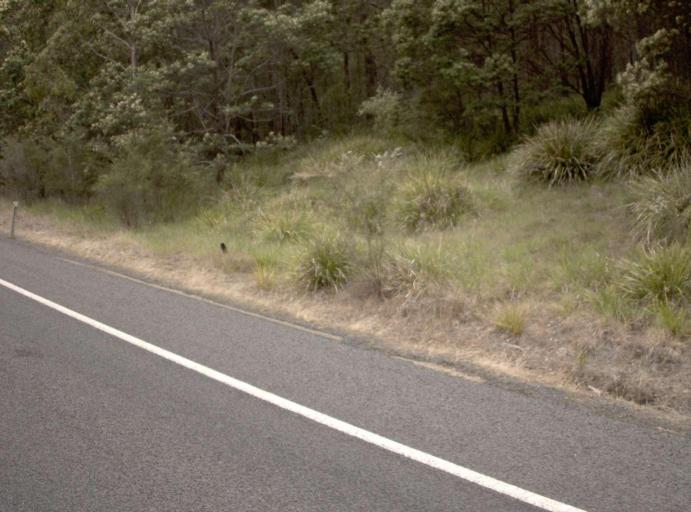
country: AU
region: New South Wales
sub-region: Bombala
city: Bombala
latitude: -37.2300
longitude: 149.2762
